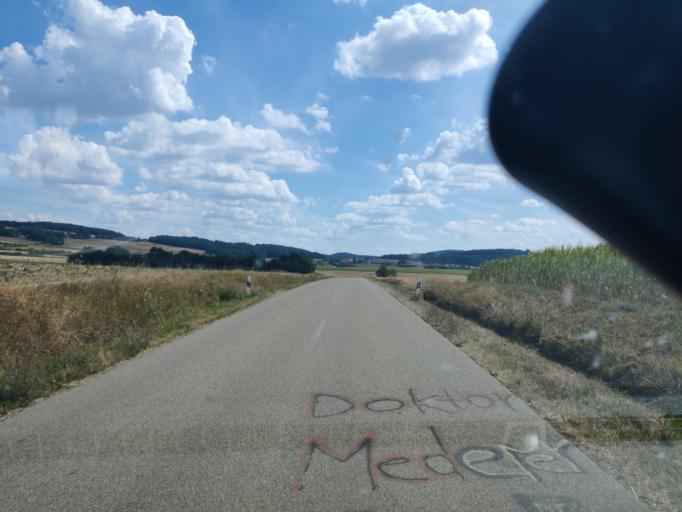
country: DE
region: Bavaria
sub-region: Regierungsbezirk Mittelfranken
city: Thalmassing
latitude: 49.1065
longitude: 11.1999
